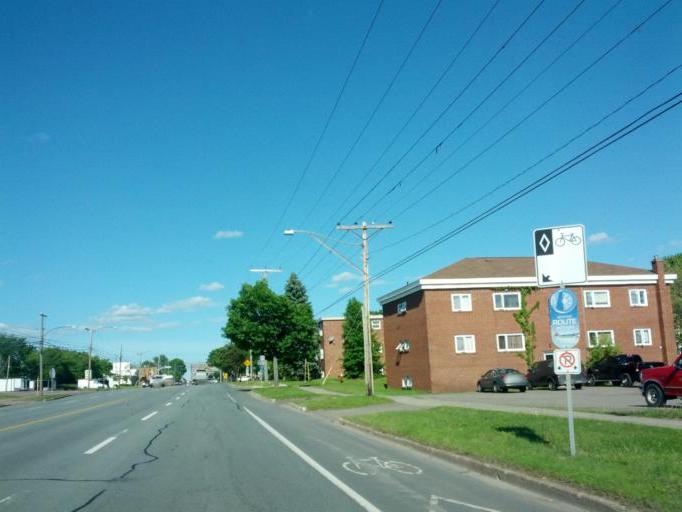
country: CA
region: New Brunswick
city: Moncton
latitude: 46.0864
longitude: -64.8038
